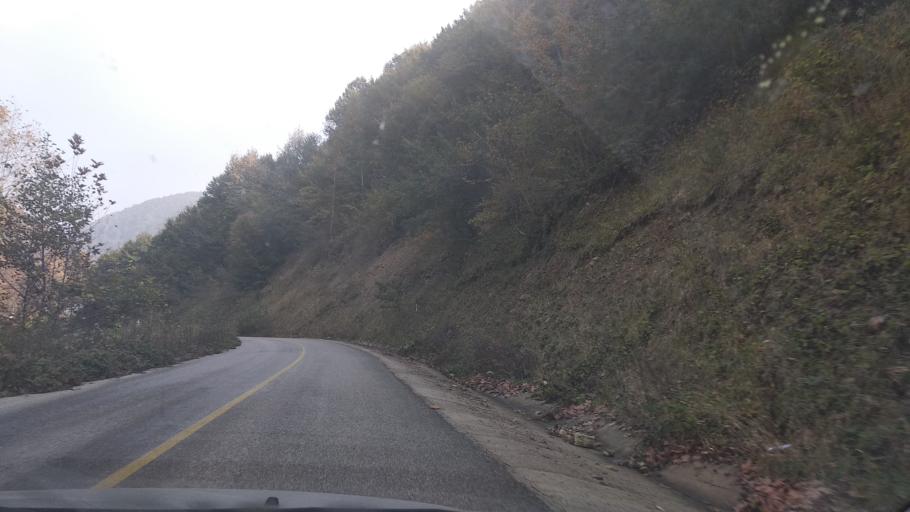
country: TR
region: Duzce
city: Kaynasli
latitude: 40.7269
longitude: 31.2475
